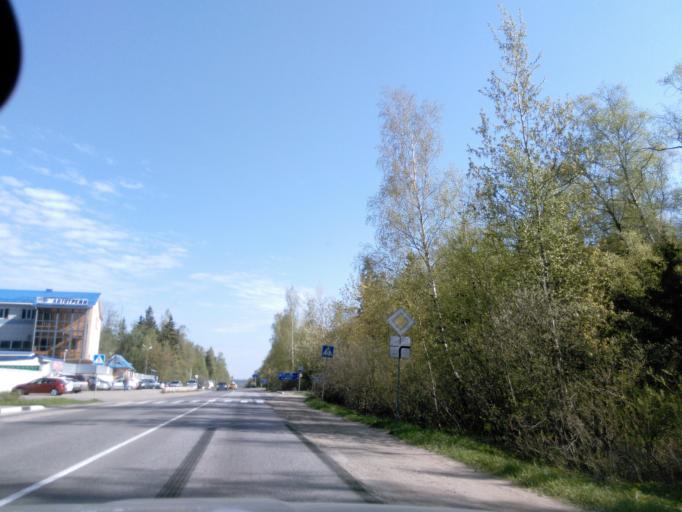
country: RU
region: Moskovskaya
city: Mendeleyevo
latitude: 56.0268
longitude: 37.2092
